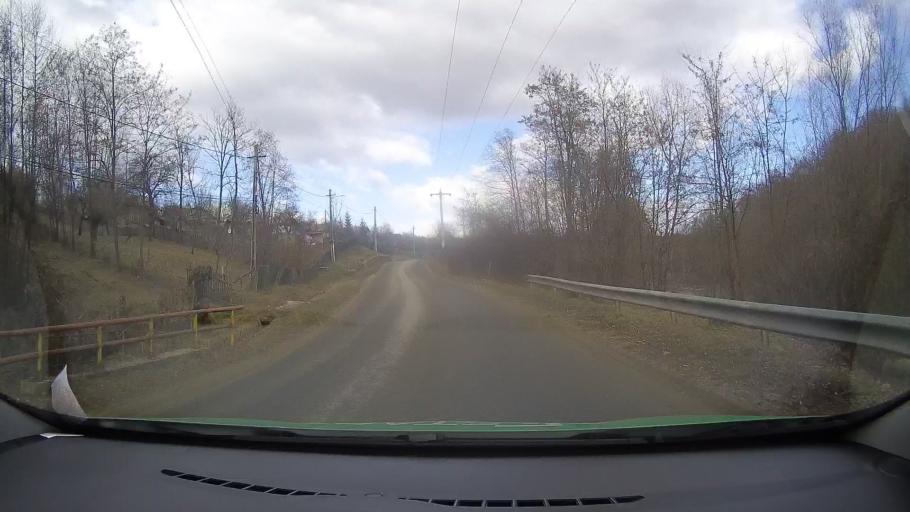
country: RO
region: Dambovita
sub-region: Comuna Buciumeni
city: Buciumeni
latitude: 45.1306
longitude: 25.4683
